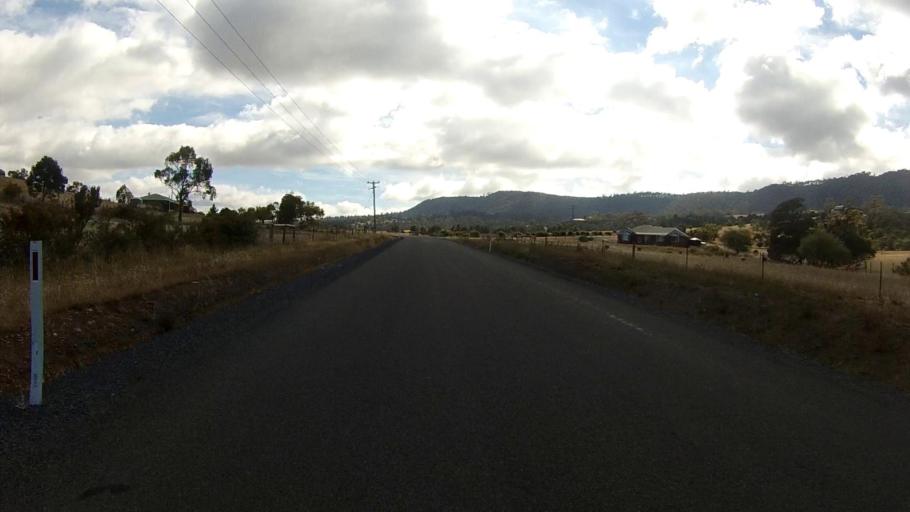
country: AU
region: Tasmania
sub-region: Brighton
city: Old Beach
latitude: -42.7671
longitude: 147.2981
